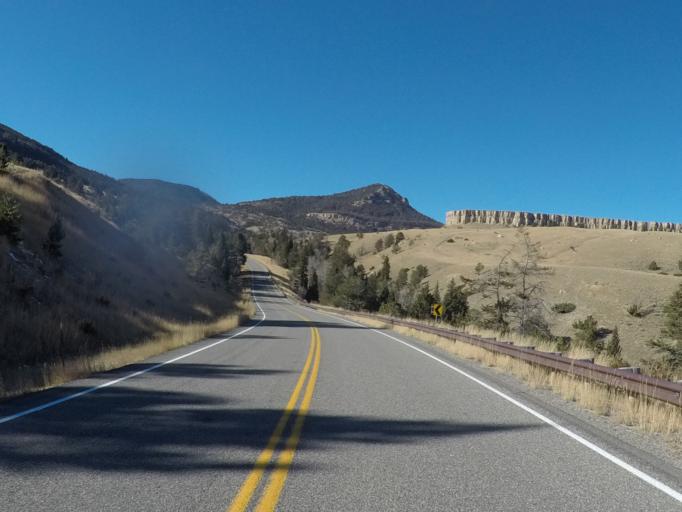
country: US
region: Montana
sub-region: Carbon County
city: Red Lodge
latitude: 44.7894
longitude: -109.4337
